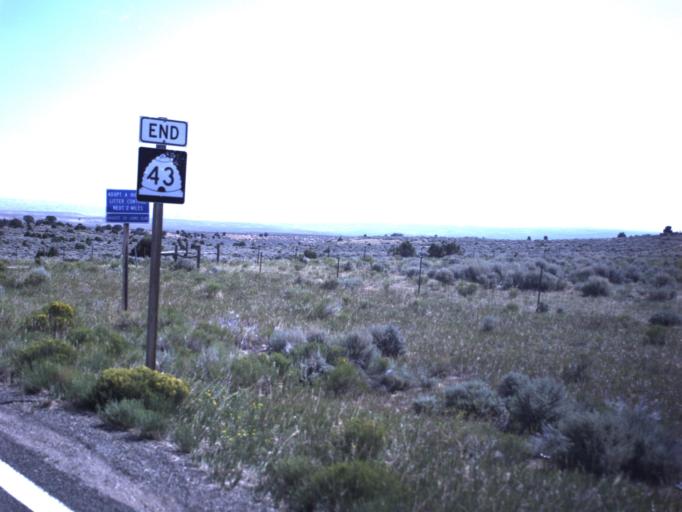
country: US
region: Utah
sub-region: Daggett County
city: Manila
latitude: 40.9974
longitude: -109.8421
